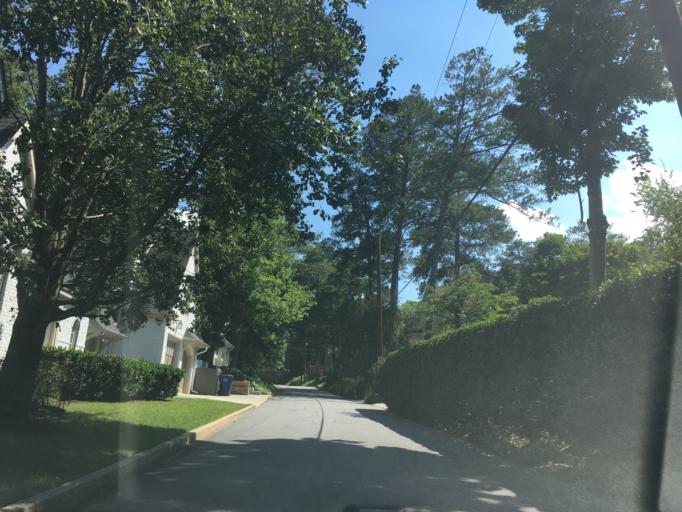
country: US
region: Georgia
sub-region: DeKalb County
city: Druid Hills
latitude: 33.7990
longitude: -84.3627
